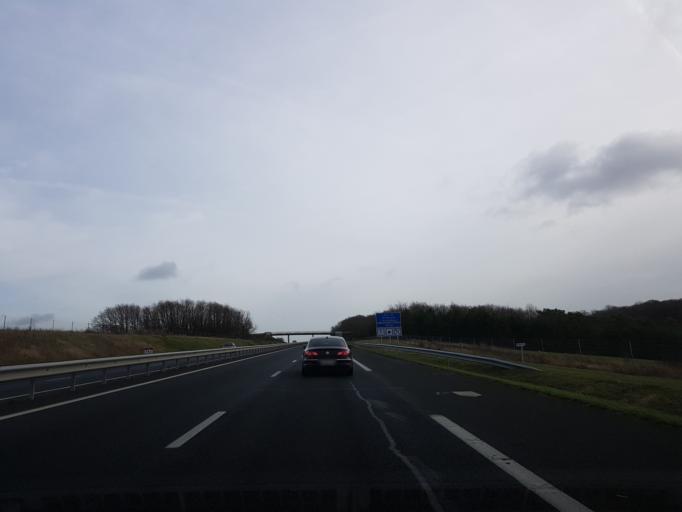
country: FR
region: Bourgogne
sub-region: Departement de l'Yonne
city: Thorigny-sur-Oreuse
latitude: 48.2354
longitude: 3.4156
